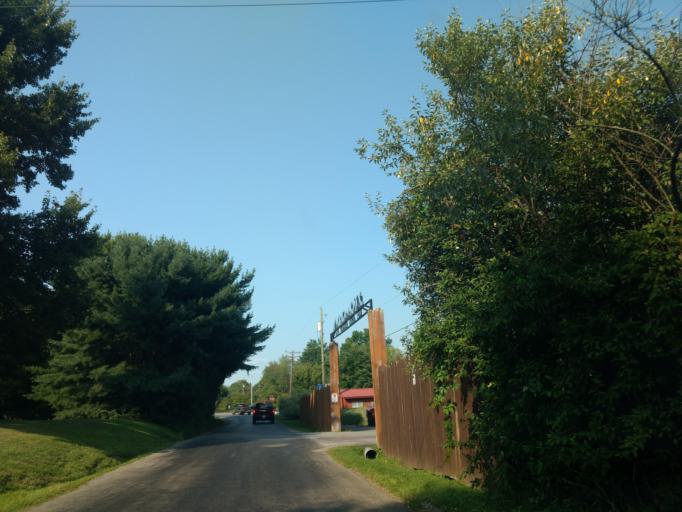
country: US
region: Pennsylvania
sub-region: Lawrence County
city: Ellport
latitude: 40.9688
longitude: -80.2163
